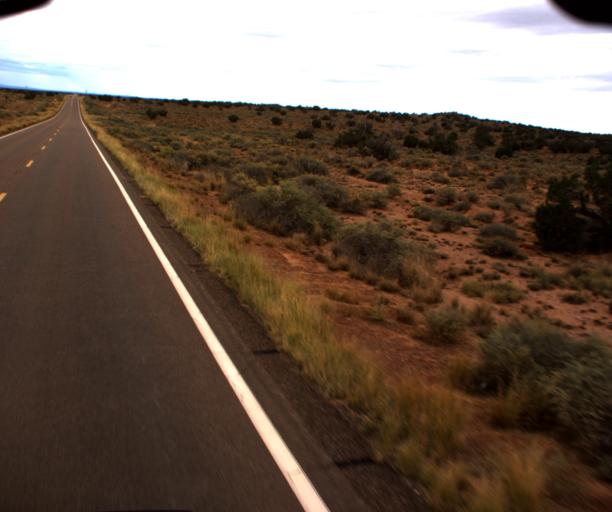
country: US
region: Arizona
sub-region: Navajo County
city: Snowflake
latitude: 34.6842
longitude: -110.1046
